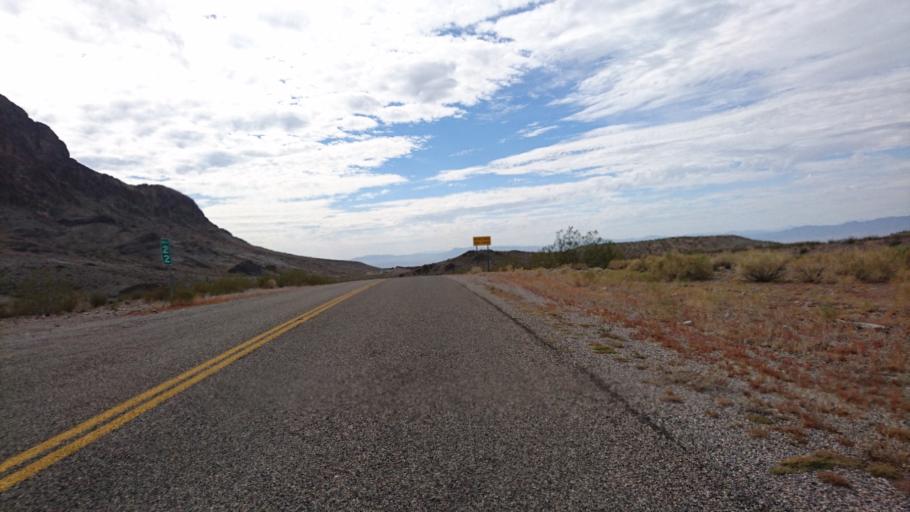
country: US
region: Arizona
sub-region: Mohave County
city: Mohave Valley
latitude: 34.9958
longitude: -114.4131
